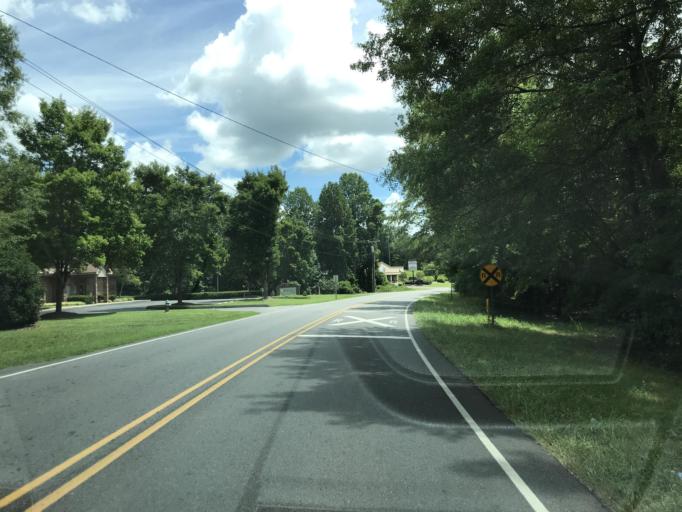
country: US
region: North Carolina
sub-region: Cleveland County
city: Shelby
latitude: 35.3063
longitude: -81.5181
